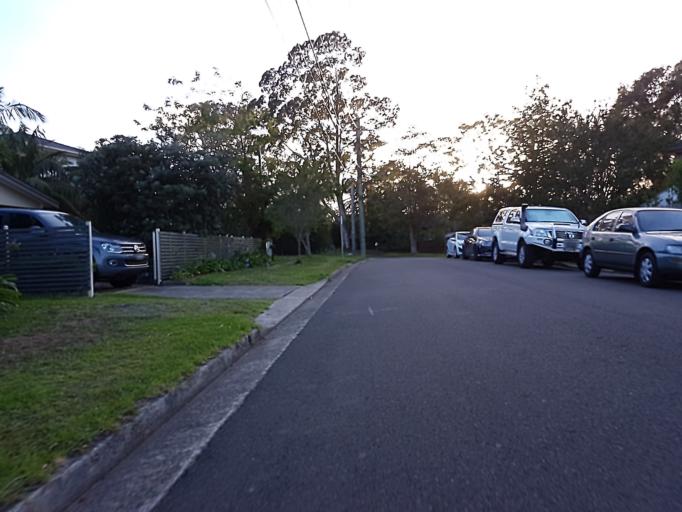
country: AU
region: New South Wales
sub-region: Warringah
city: Killarney Heights
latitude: -33.7524
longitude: 151.2300
